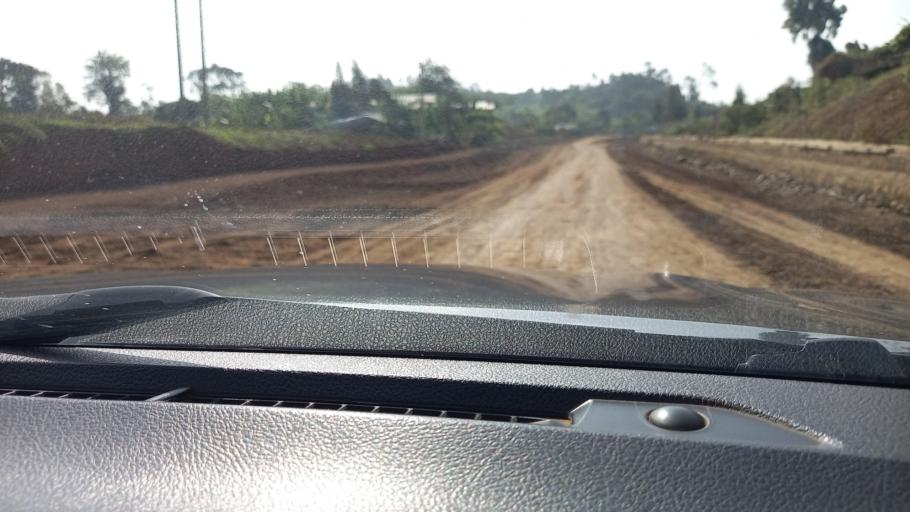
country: ET
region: Southern Nations, Nationalities, and People's Region
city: Mizan Teferi
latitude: 6.1649
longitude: 35.5917
